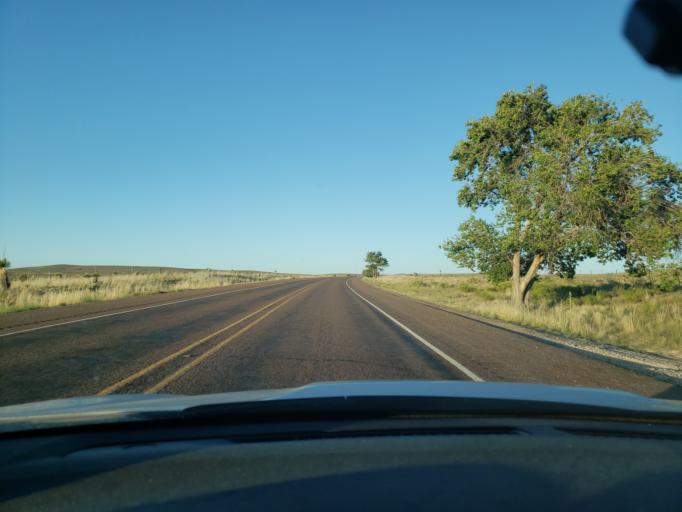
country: US
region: Texas
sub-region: El Paso County
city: Homestead Meadows South
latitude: 31.8326
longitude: -105.8606
